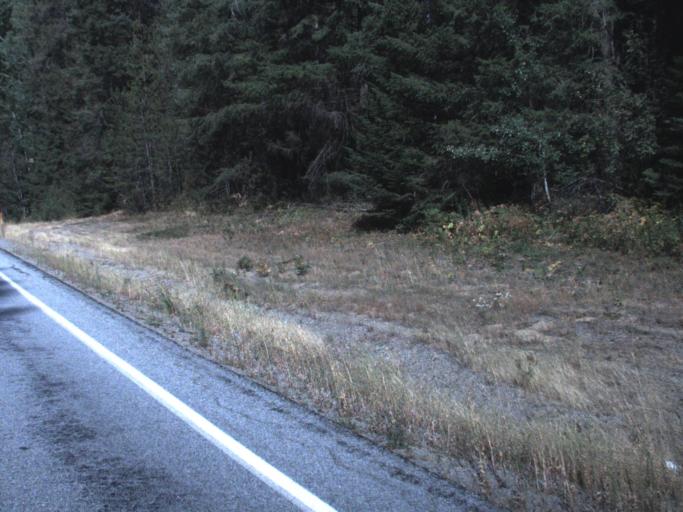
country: US
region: Washington
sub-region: Pend Oreille County
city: Newport
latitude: 48.1098
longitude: -117.2769
